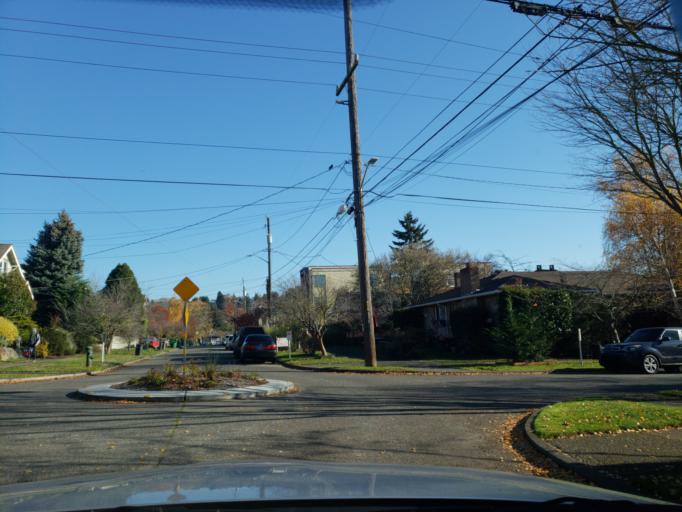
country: US
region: Washington
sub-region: King County
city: Seattle
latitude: 47.6738
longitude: -122.3689
